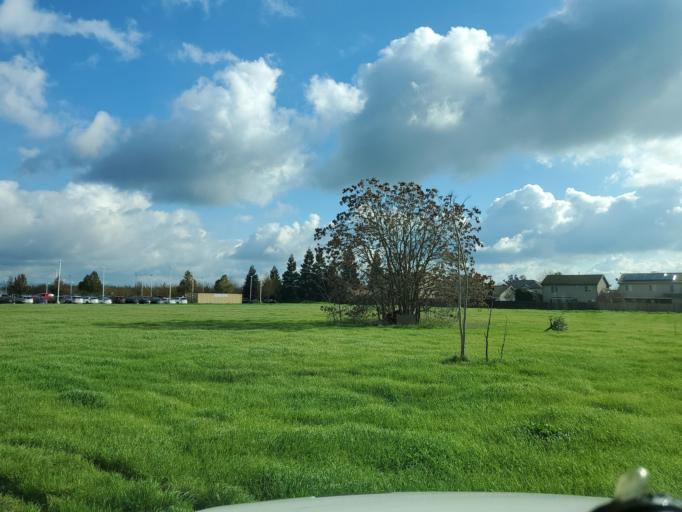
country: US
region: California
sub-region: San Joaquin County
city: Morada
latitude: 38.0167
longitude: -121.2732
